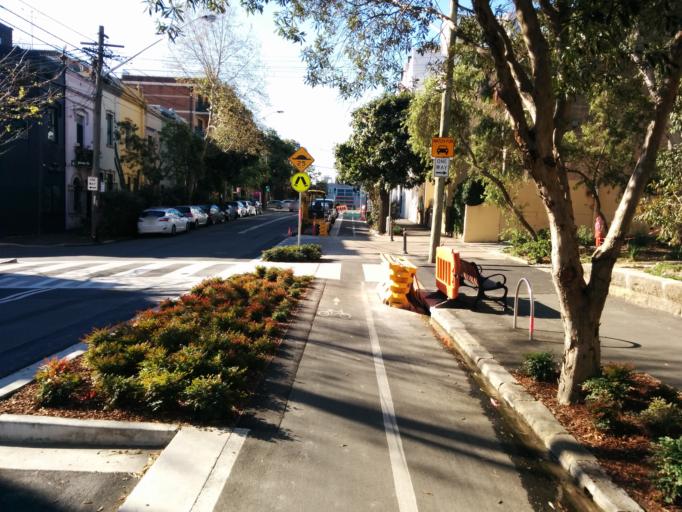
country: AU
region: New South Wales
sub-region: City of Sydney
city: Redfern
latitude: -33.8902
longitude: 151.2027
